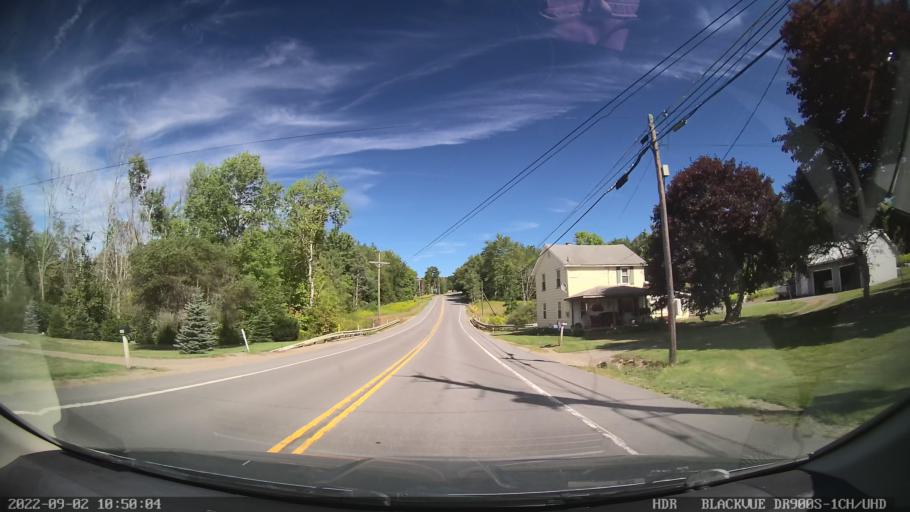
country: US
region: Pennsylvania
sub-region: Tioga County
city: Blossburg
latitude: 41.6087
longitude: -77.1162
